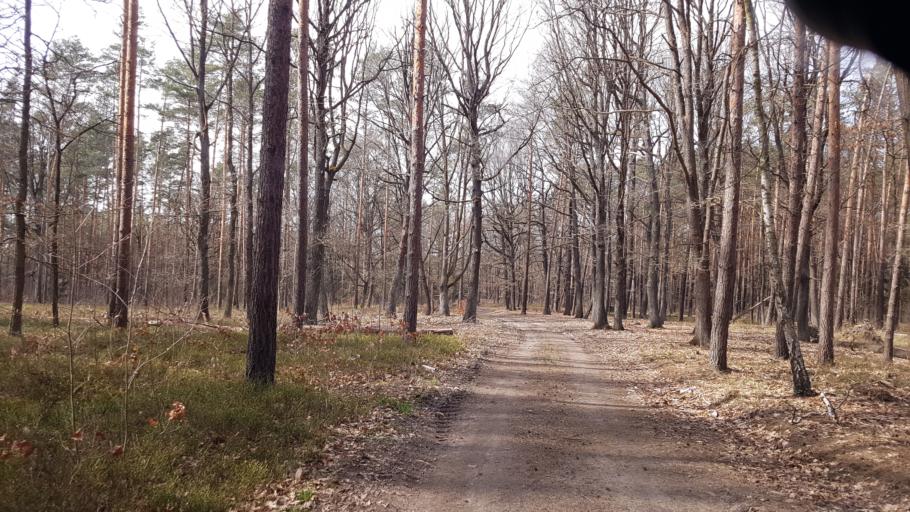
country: DE
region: Brandenburg
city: Lauchhammer
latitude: 51.5384
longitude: 13.7013
